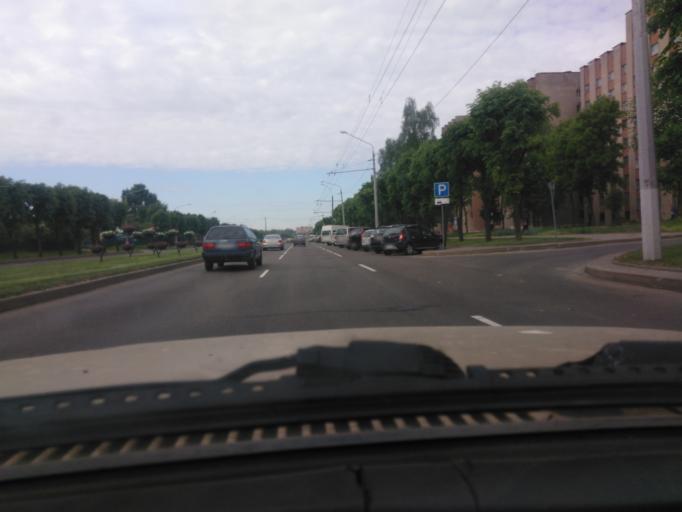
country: BY
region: Mogilev
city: Mahilyow
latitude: 53.9074
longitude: 30.3091
